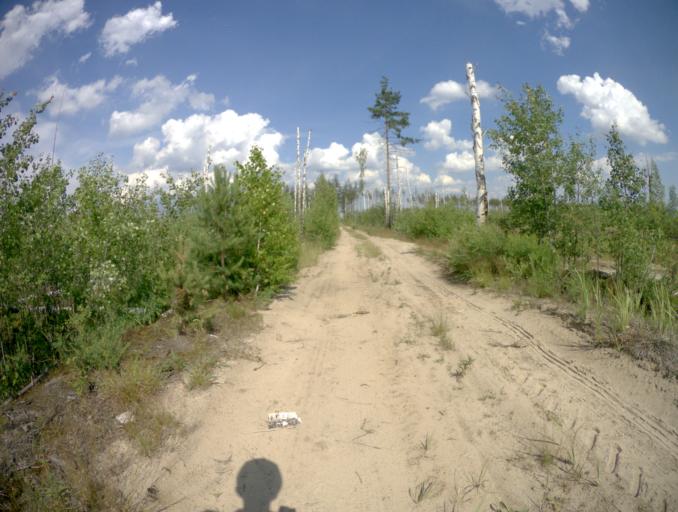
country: RU
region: Ivanovo
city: Talitsy
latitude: 56.5301
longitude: 42.2324
